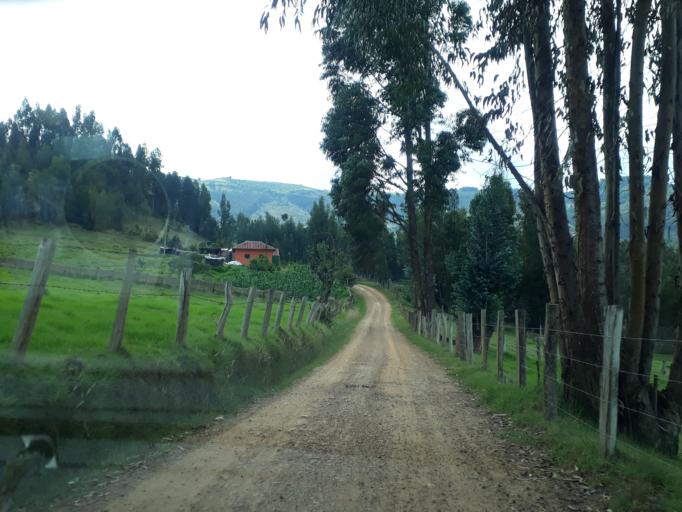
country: CO
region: Boyaca
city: Santa Rosa de Viterbo
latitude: 5.8502
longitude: -72.9591
